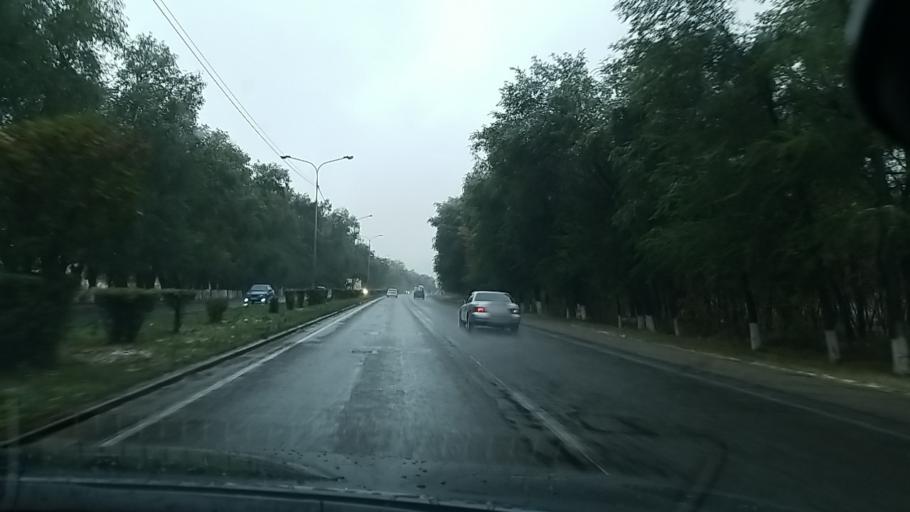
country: KZ
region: Almaty Oblysy
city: Burunday
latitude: 43.2187
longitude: 76.7081
